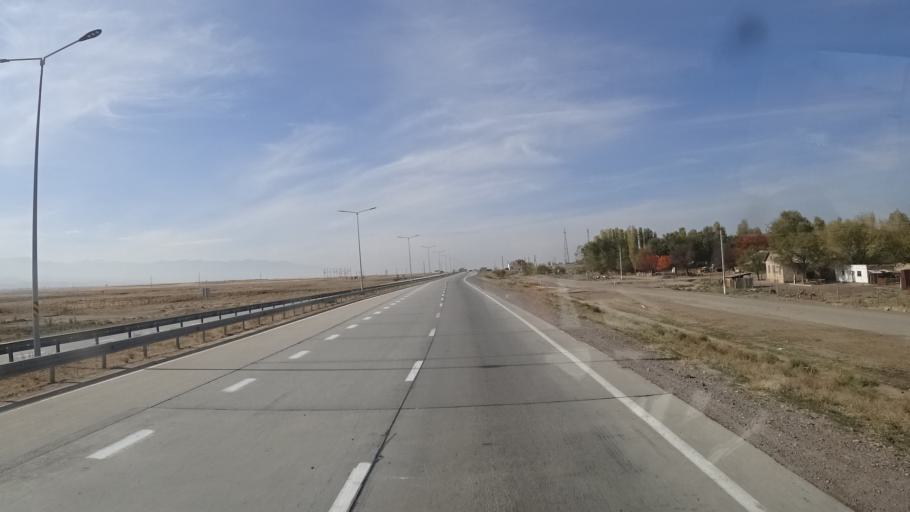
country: KZ
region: Zhambyl
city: Merke
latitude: 42.8888
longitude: 72.9927
